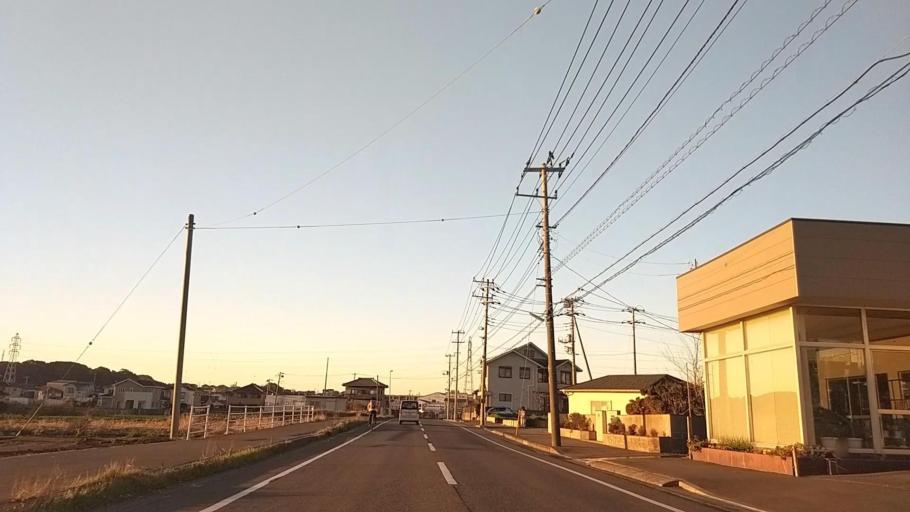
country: JP
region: Chiba
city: Hasaki
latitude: 35.7170
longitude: 140.8380
